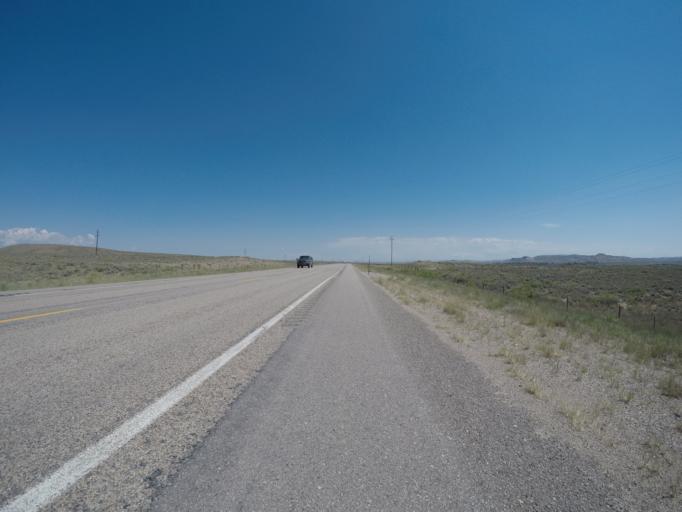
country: US
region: Wyoming
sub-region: Sublette County
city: Marbleton
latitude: 42.4021
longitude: -110.1221
